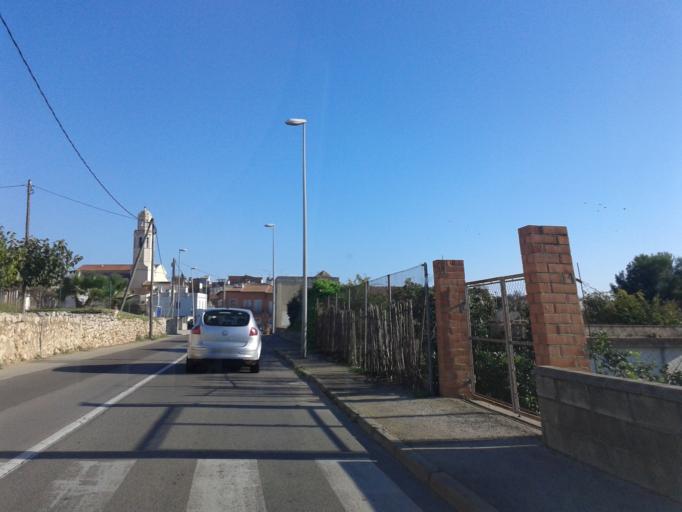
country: ES
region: Catalonia
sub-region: Provincia de Barcelona
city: Cubelles
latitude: 41.2101
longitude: 1.6707
